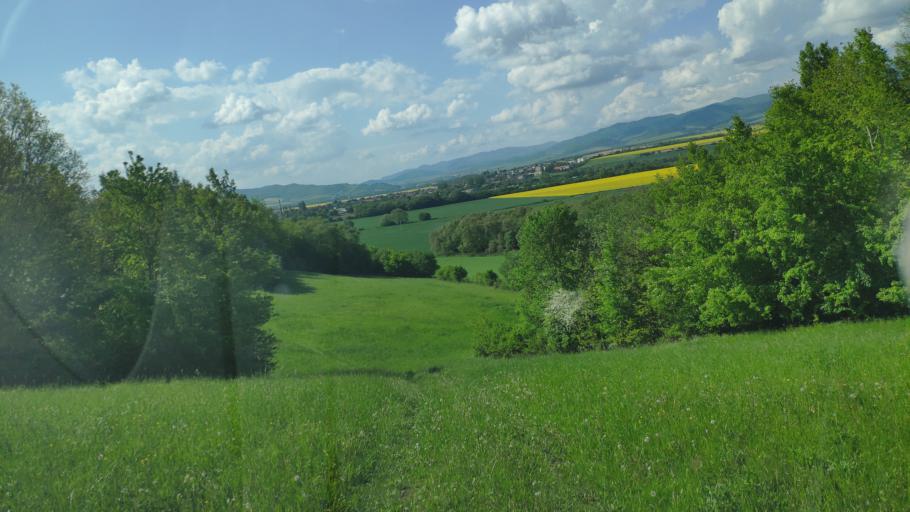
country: SK
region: Presovsky
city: Sabinov
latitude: 49.0519
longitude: 21.1519
